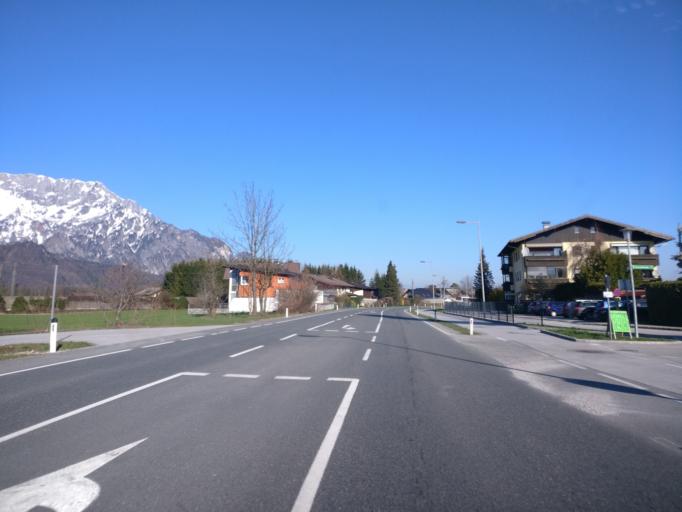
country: AT
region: Salzburg
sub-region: Politischer Bezirk Hallein
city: Oberalm
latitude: 47.7055
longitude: 13.0944
